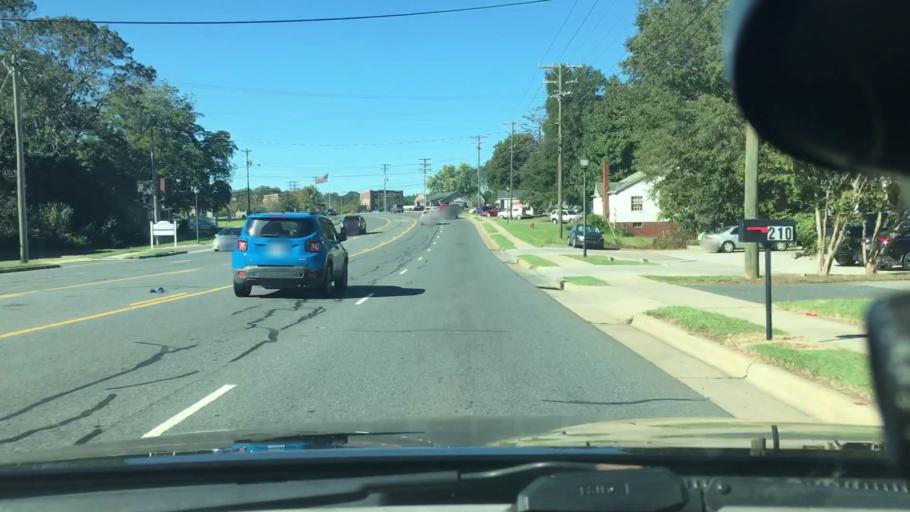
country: US
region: North Carolina
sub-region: Stanly County
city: Locust
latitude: 35.2598
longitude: -80.4276
